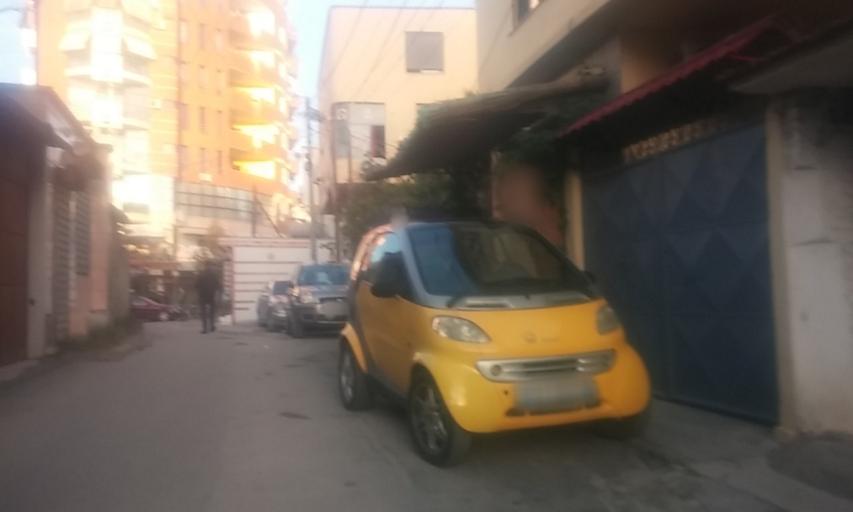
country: AL
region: Tirane
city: Tirana
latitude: 41.3202
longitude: 19.8286
